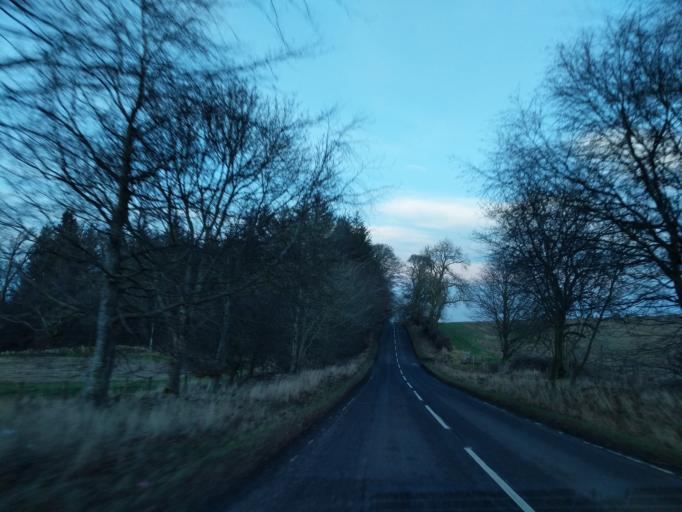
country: GB
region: Scotland
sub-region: Midlothian
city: Bonnyrigg
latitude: 55.8108
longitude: -3.1073
